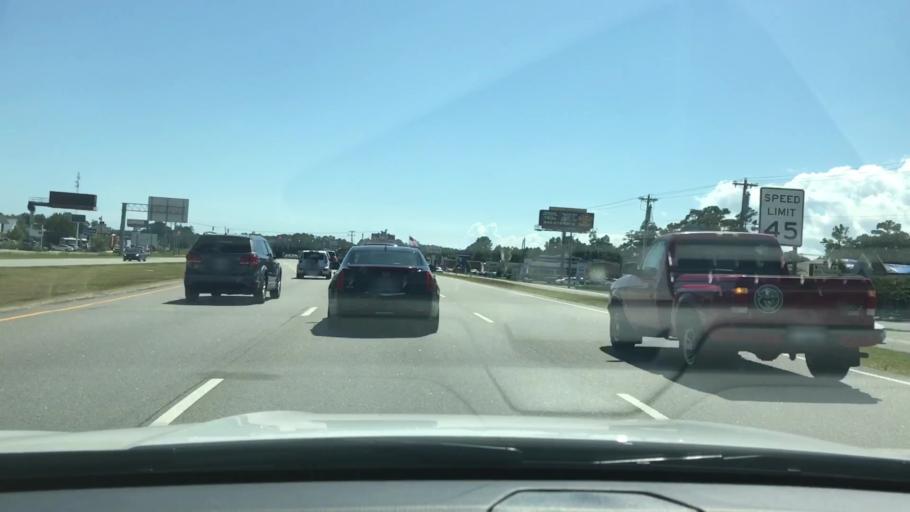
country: US
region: South Carolina
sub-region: Horry County
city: Socastee
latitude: 33.6807
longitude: -78.9640
